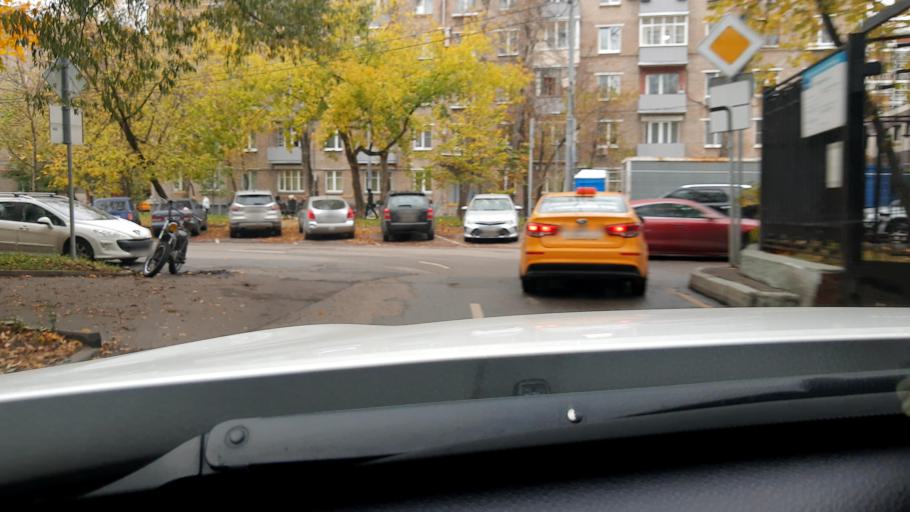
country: RU
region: Moscow
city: Sokol
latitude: 55.8072
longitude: 37.5393
